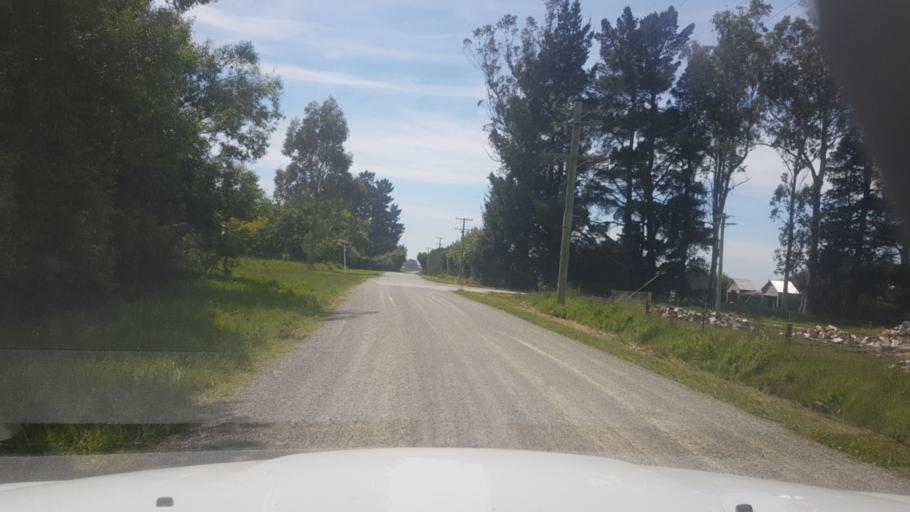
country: NZ
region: Canterbury
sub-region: Timaru District
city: Pleasant Point
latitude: -44.2457
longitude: 171.1811
